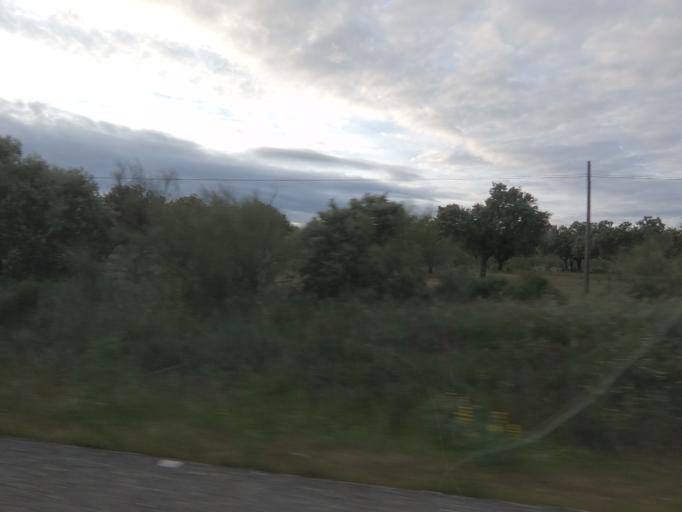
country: ES
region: Extremadura
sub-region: Provincia de Badajoz
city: La Roca de la Sierra
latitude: 39.1217
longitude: -6.6732
